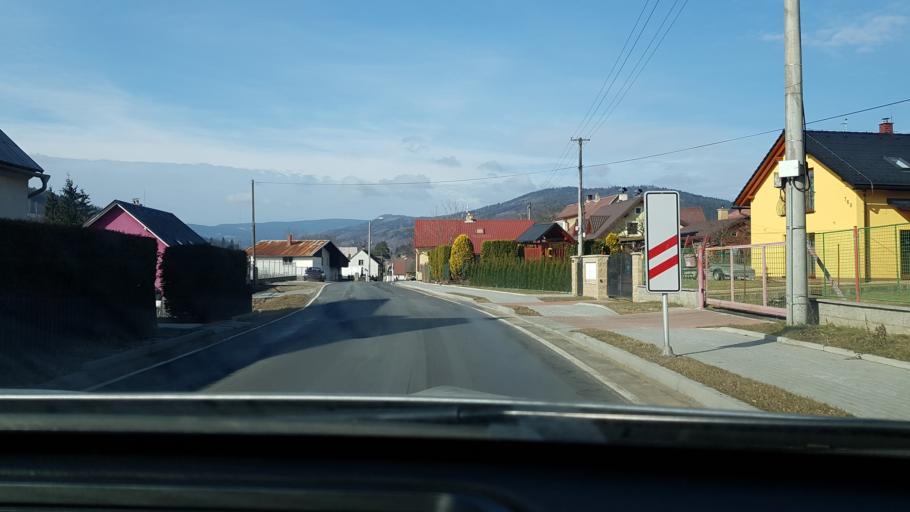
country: CZ
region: Olomoucky
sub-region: Okres Jesenik
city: Jesenik
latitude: 50.2286
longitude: 17.1659
